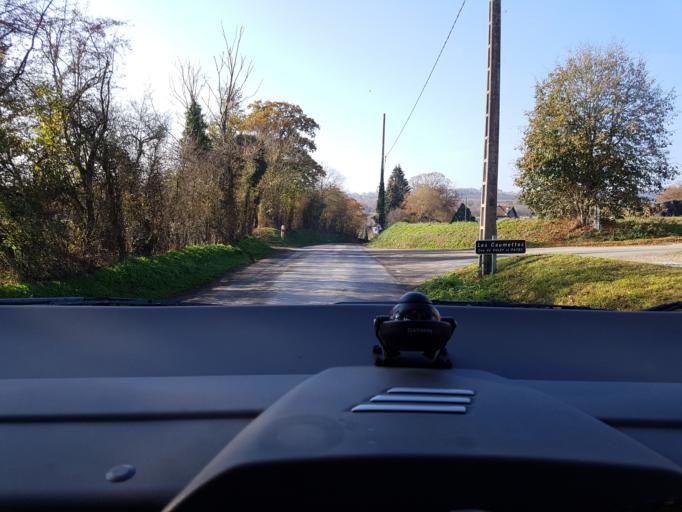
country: FR
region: Lower Normandy
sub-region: Departement du Calvados
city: Saint-Remy
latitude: 48.9466
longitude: -0.5124
